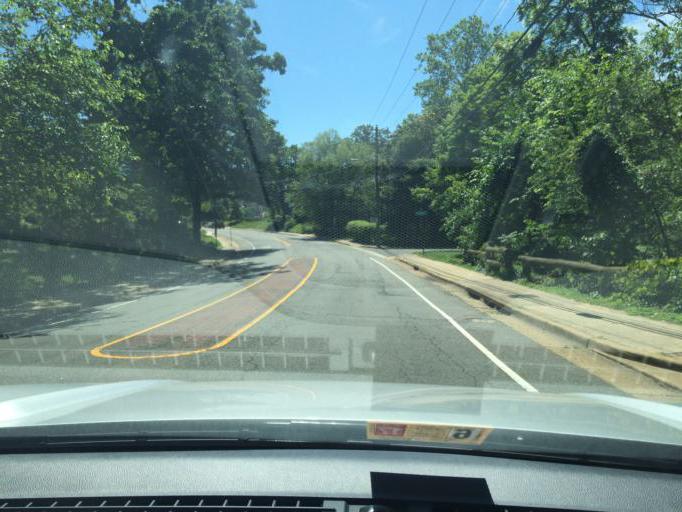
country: US
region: Virginia
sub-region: Fairfax County
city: Huntington
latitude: 38.8255
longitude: -77.0777
